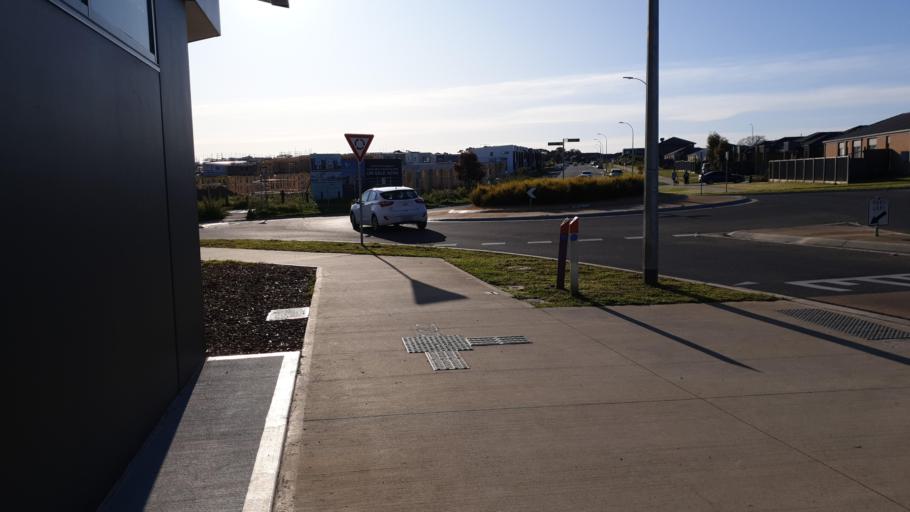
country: AU
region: Victoria
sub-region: Casey
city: Junction Village
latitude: -38.1493
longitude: 145.2894
